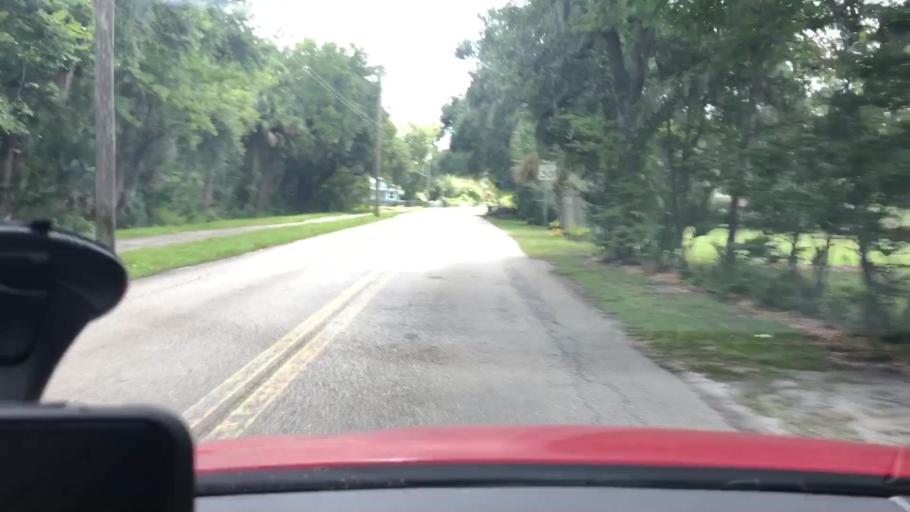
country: US
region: Florida
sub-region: Volusia County
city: New Smyrna Beach
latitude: 29.0108
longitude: -80.9254
